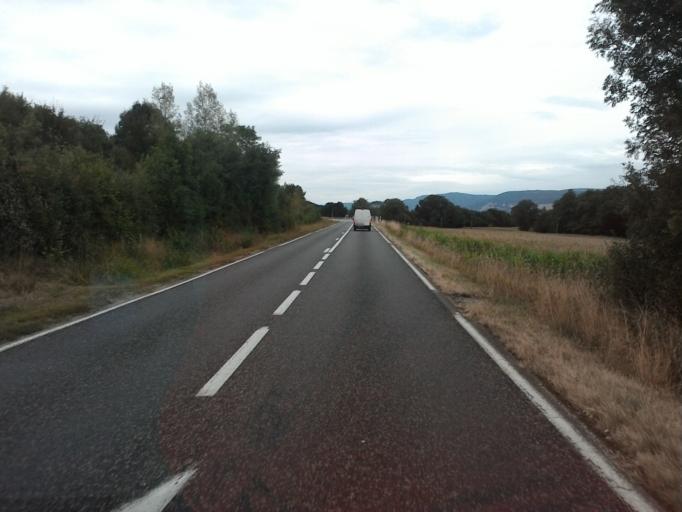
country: FR
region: Rhone-Alpes
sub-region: Departement de l'Isere
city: Bouvesse-Quirieu
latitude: 45.7617
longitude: 5.4037
